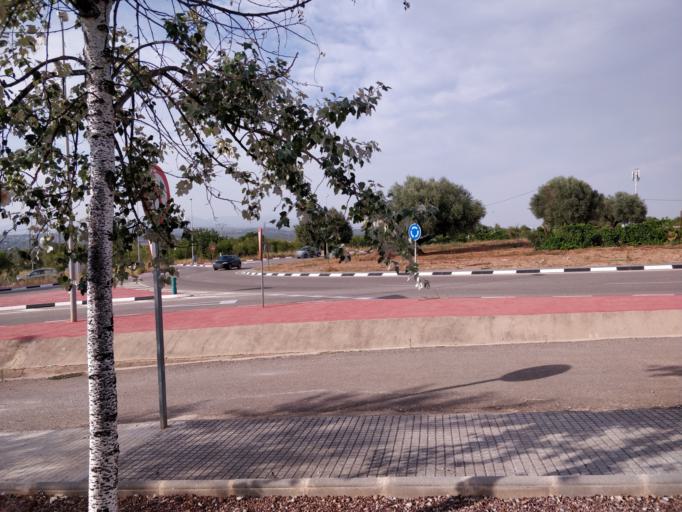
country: ES
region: Valencia
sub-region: Provincia de Castello
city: Villafames
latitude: 40.1187
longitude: -0.0535
